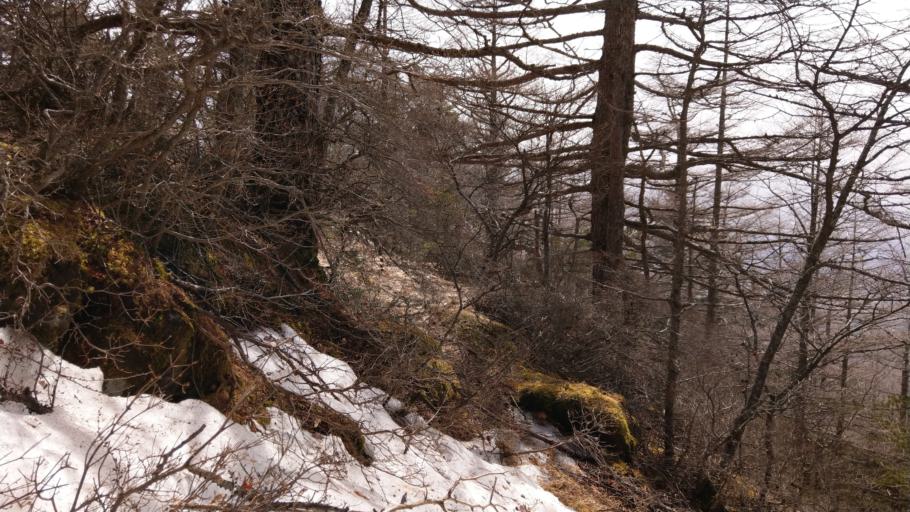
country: JP
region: Nagano
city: Komoro
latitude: 36.3949
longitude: 138.4531
